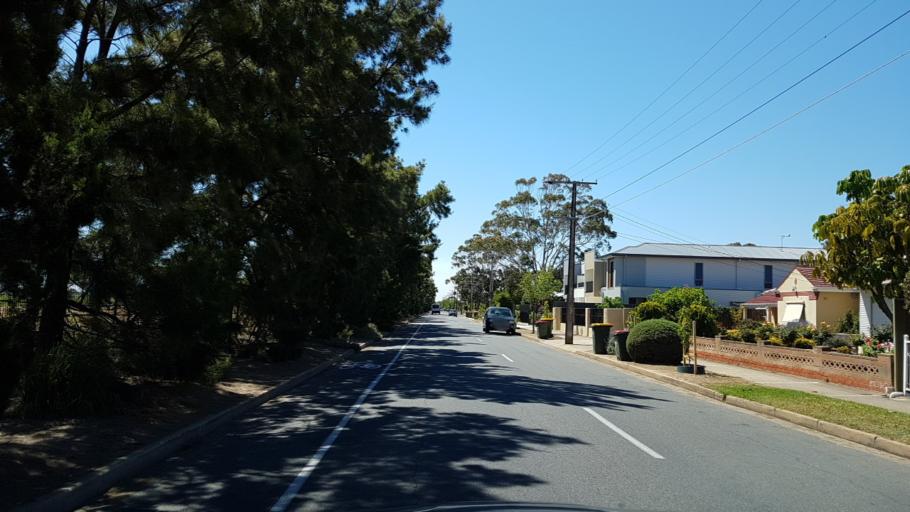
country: AU
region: South Australia
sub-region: Marion
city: Plympton Park
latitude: -34.9801
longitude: 138.5471
